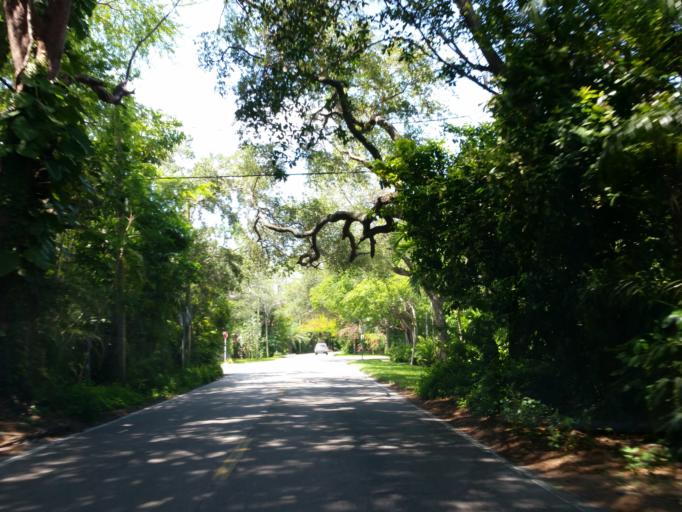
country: US
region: Florida
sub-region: Miami-Dade County
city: Coconut Grove
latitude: 25.7101
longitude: -80.2562
